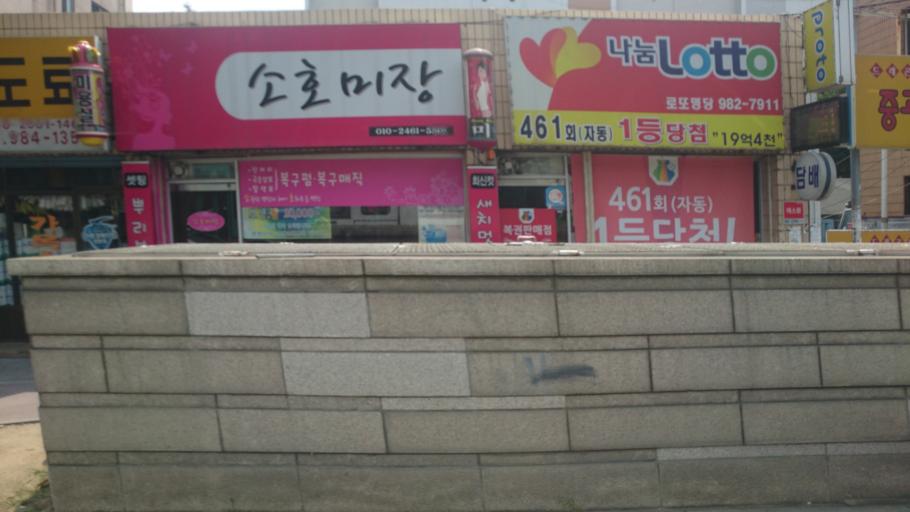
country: KR
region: Gyeongsangbuk-do
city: Gyeongsan-si
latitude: 35.8778
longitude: 128.6762
